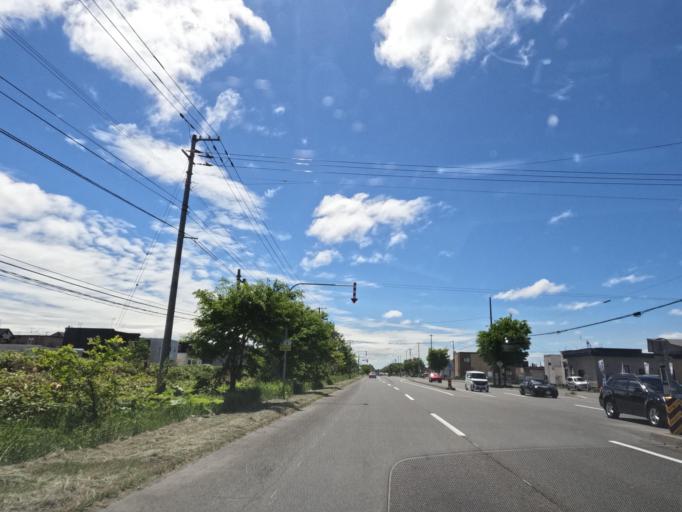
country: JP
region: Hokkaido
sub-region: Asahikawa-shi
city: Asahikawa
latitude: 43.7411
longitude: 142.3597
